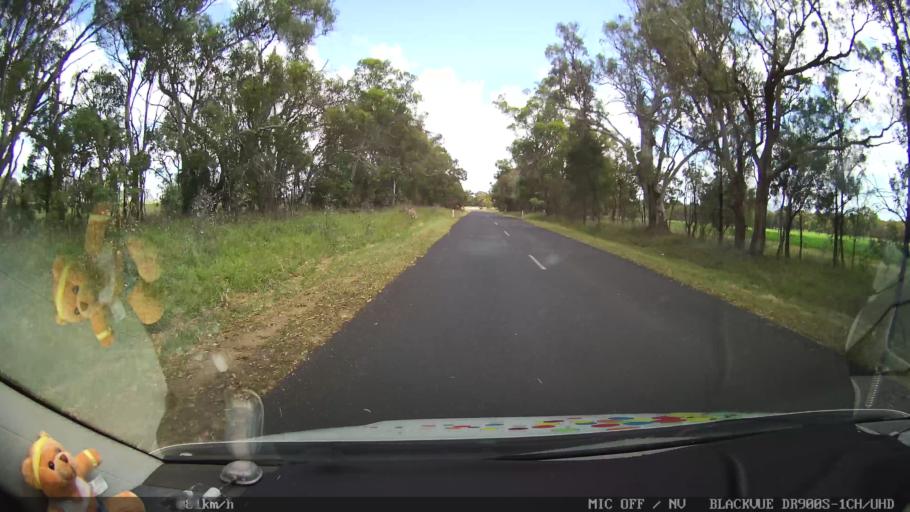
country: AU
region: New South Wales
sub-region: Glen Innes Severn
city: Glen Innes
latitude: -29.4785
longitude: 151.6824
